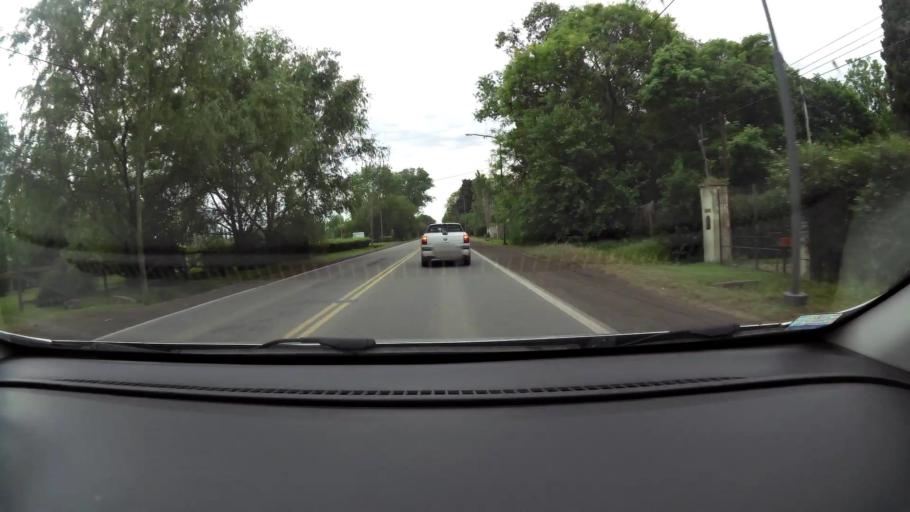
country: AR
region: Buenos Aires
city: San Nicolas de los Arroyos
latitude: -33.3801
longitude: -60.2111
